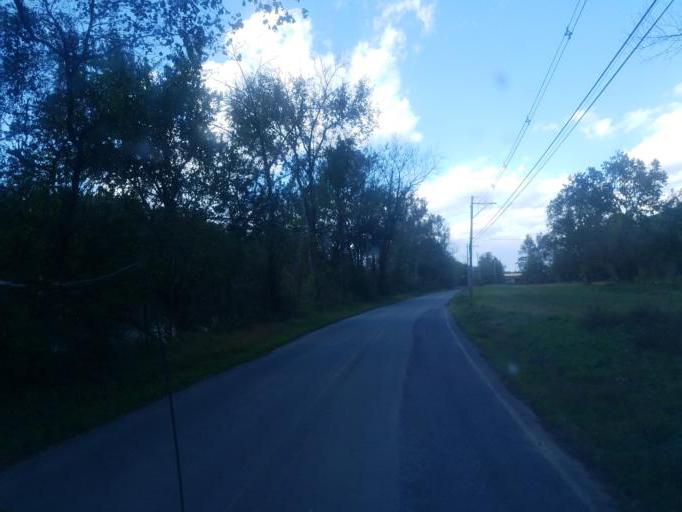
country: US
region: Pennsylvania
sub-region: Dauphin County
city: Middletown
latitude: 40.2068
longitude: -76.7140
